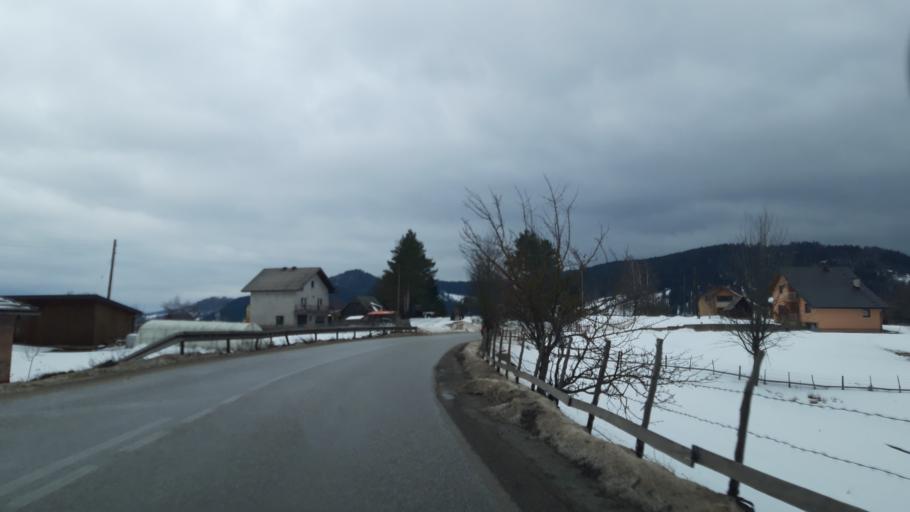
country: BA
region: Republika Srpska
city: Pale
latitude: 43.8919
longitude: 18.6271
